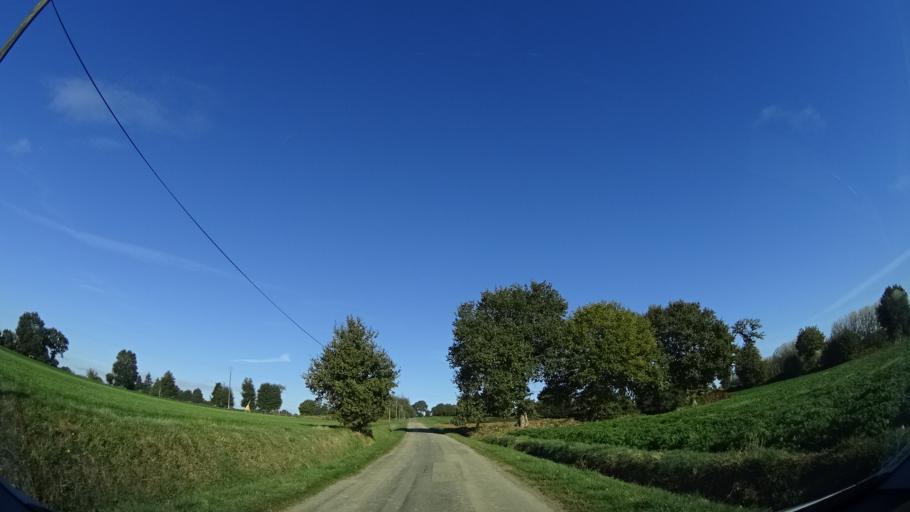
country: FR
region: Brittany
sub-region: Departement d'Ille-et-Vilaine
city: Geveze
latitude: 48.2001
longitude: -1.7792
